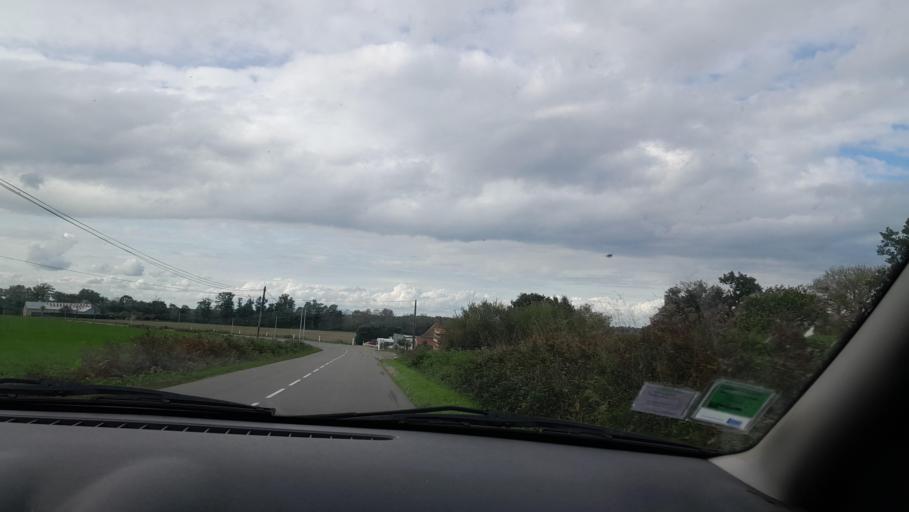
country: FR
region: Brittany
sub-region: Departement d'Ille-et-Vilaine
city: Argentre-du-Plessis
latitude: 48.0498
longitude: -1.0942
